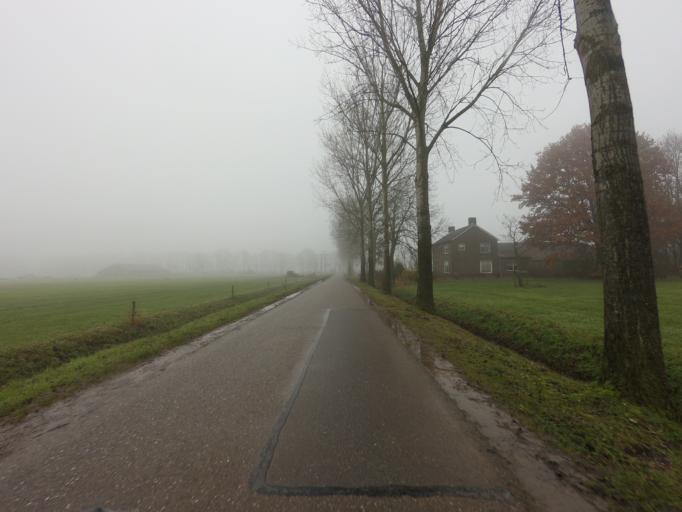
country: NL
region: Gelderland
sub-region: Gemeente Zaltbommel
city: Nederhemert-Noord
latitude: 51.7707
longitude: 5.1746
